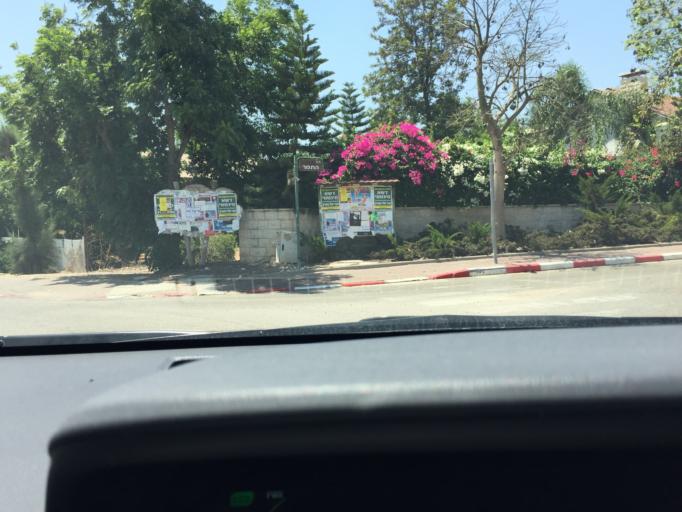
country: IL
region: Central District
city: Nehalim
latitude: 32.0509
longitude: 34.9023
